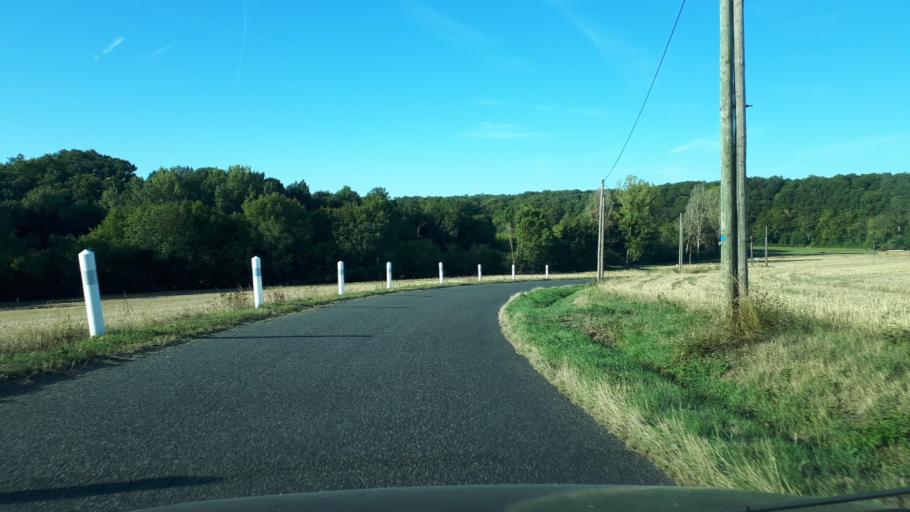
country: FR
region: Centre
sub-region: Departement d'Indre-et-Loire
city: Chateau-Renault
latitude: 47.6571
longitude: 0.9413
